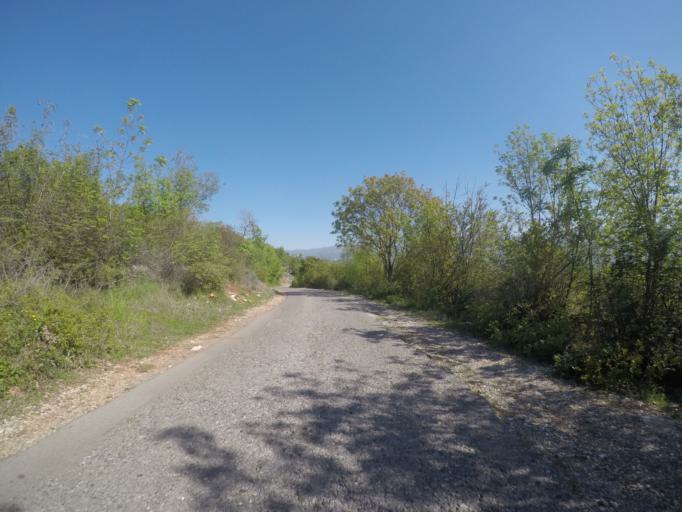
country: ME
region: Danilovgrad
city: Danilovgrad
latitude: 42.5244
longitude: 19.0949
